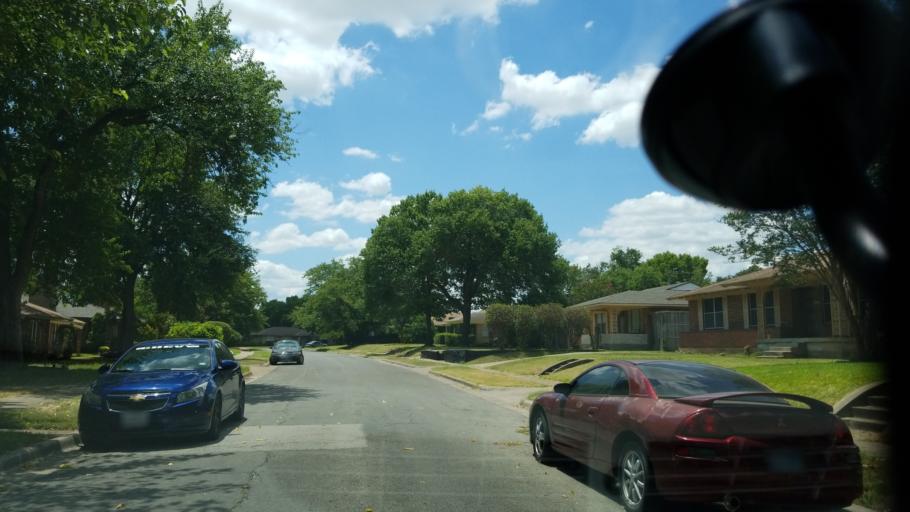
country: US
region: Texas
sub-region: Dallas County
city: Cockrell Hill
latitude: 32.7079
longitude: -96.8474
